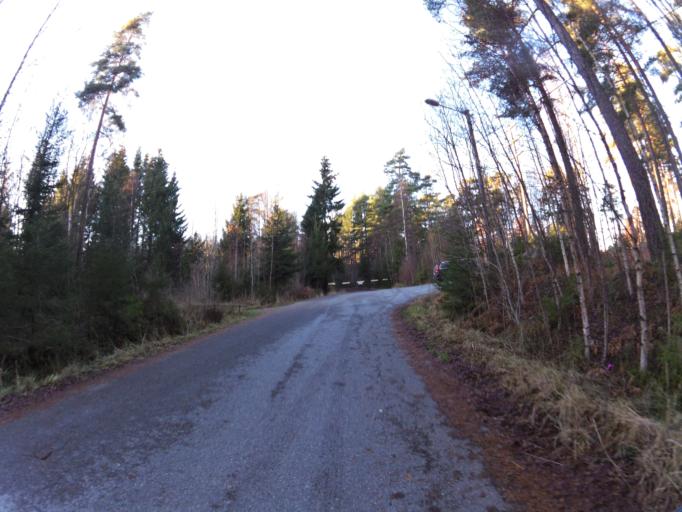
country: NO
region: Ostfold
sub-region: Fredrikstad
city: Fredrikstad
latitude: 59.2413
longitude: 10.9647
